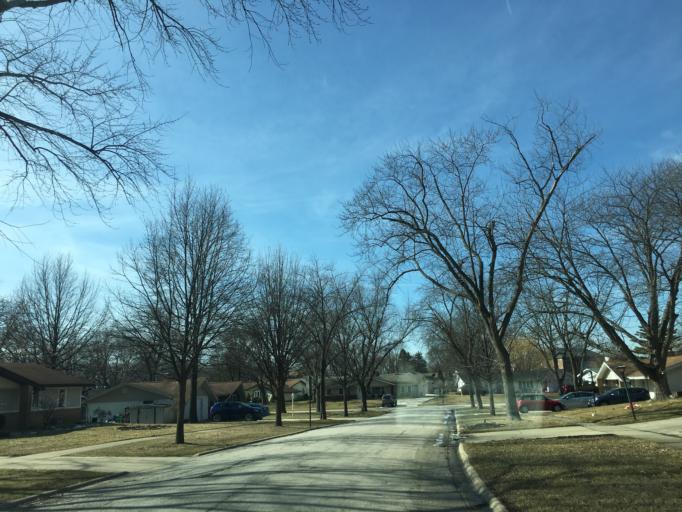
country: US
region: Illinois
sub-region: DuPage County
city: Hanover Park
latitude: 42.0198
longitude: -88.1249
